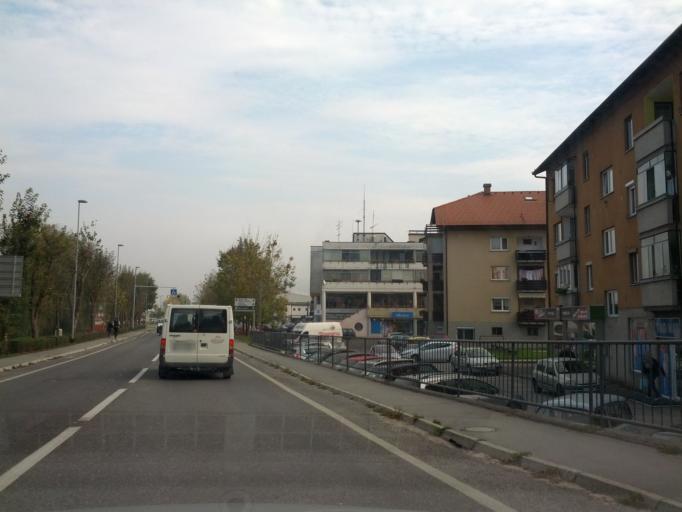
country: SI
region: Litija
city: Litija
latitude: 46.0568
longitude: 14.8294
